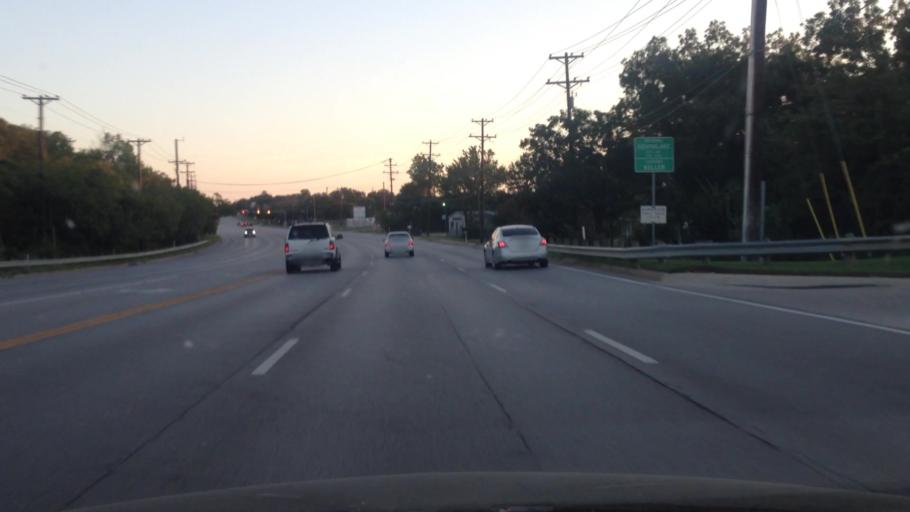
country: US
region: Texas
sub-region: Tarrant County
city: Colleyville
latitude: 32.9238
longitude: -97.1862
